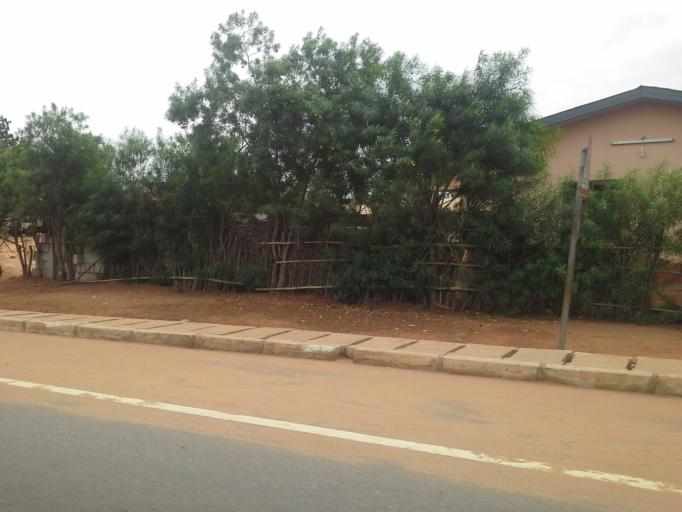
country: GH
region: Volta
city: Keta
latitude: 6.0644
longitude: 0.9175
